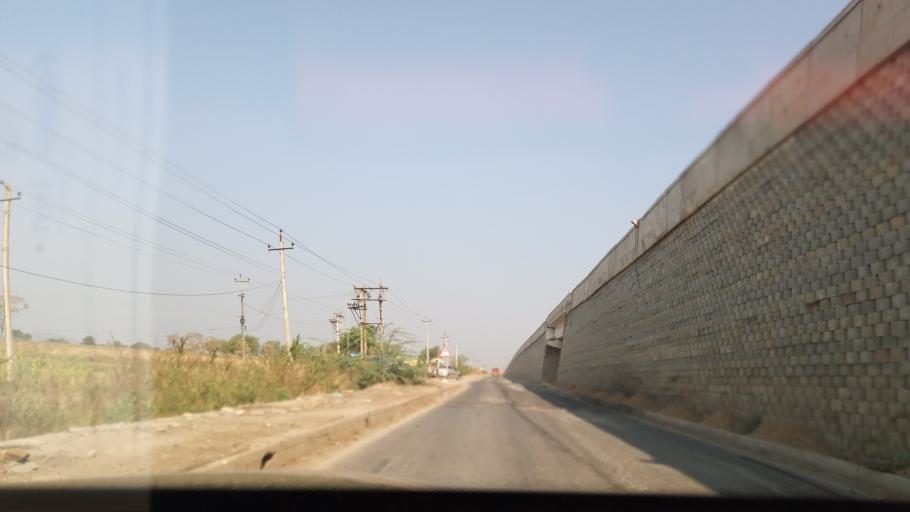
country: IN
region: Karnataka
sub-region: Haveri
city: Savanur
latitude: 14.8828
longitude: 75.3074
